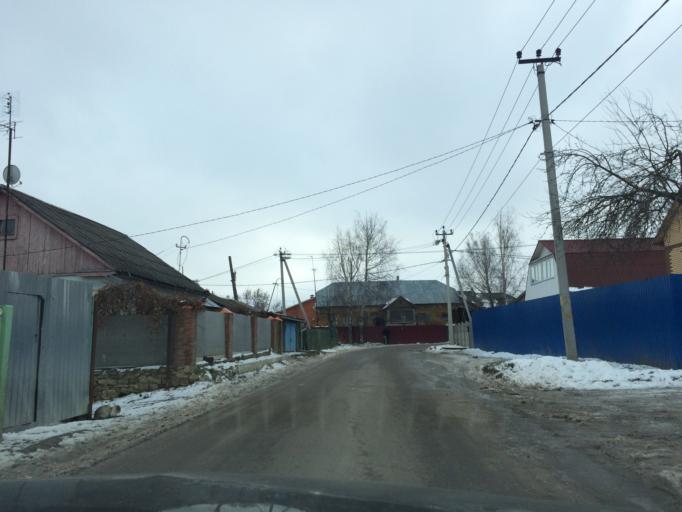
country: RU
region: Tula
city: Plavsk
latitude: 53.7068
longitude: 37.2978
